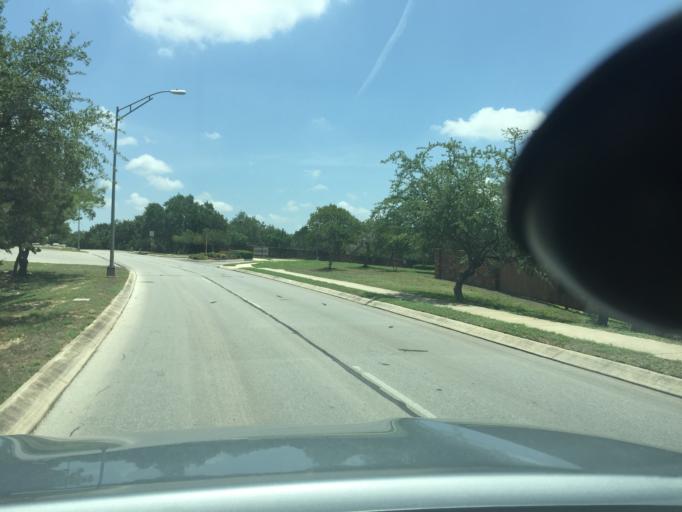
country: US
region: Texas
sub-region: Bexar County
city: Timberwood Park
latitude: 29.6847
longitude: -98.4692
